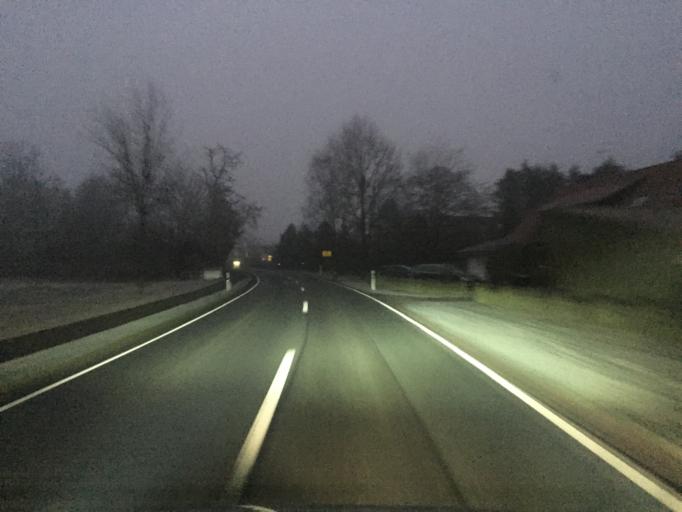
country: DE
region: Lower Saxony
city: Borstel
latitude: 52.5997
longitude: 8.9466
